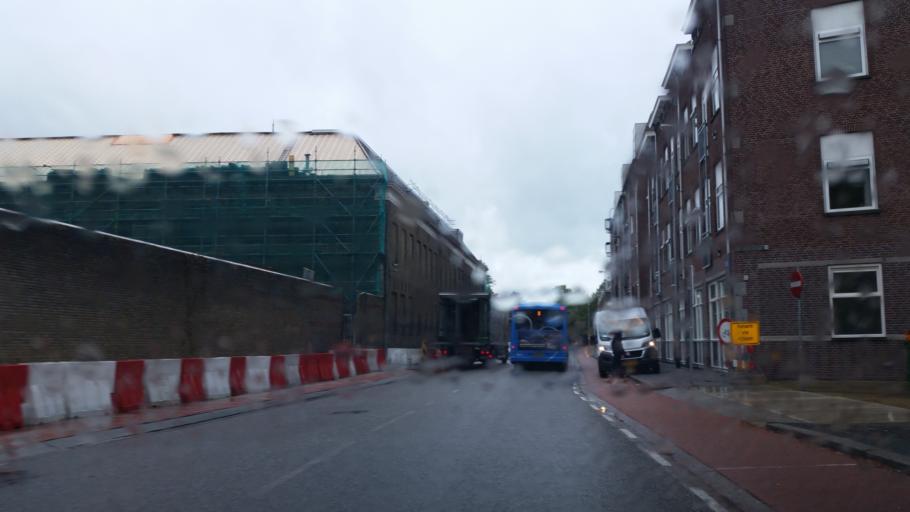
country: NL
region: Friesland
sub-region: Gemeente Leeuwarden
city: Leeuwarden
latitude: 53.2003
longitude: 5.8022
